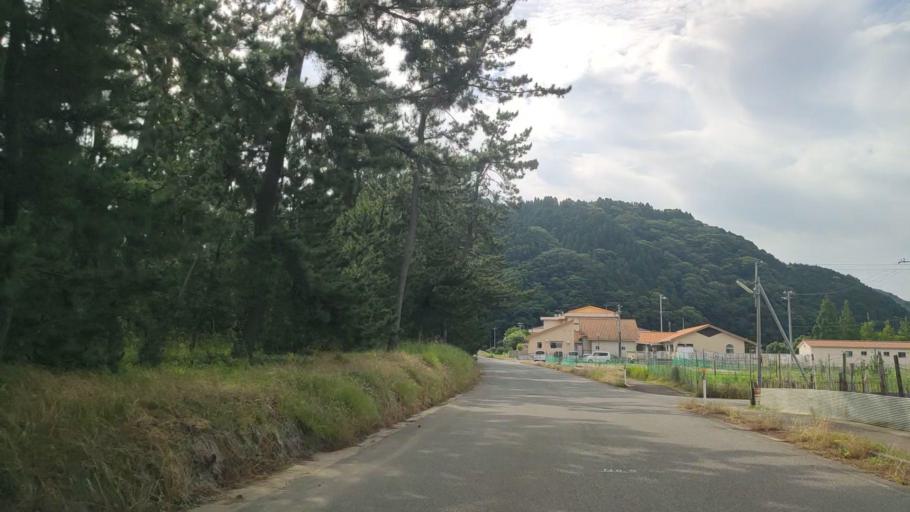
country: JP
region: Hyogo
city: Toyooka
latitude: 35.6424
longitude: 134.8375
